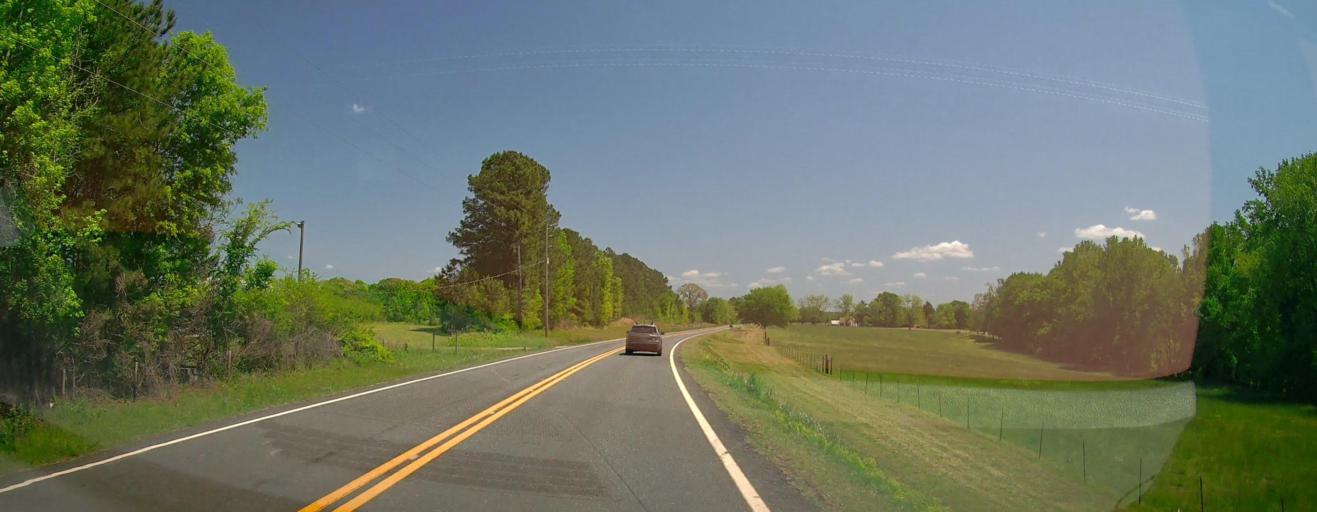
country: US
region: Georgia
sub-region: Jasper County
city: Monticello
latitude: 33.2906
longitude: -83.6346
